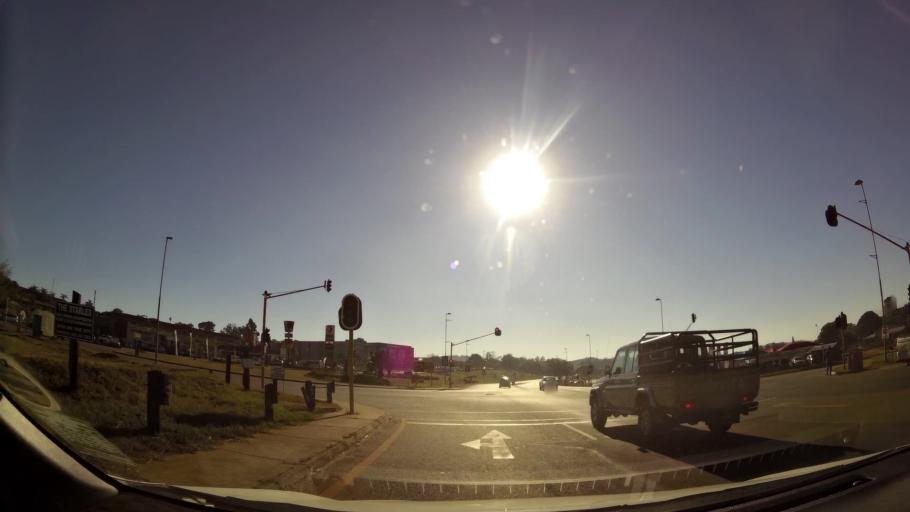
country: ZA
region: Limpopo
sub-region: Mopani District Municipality
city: Tzaneen
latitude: -23.8254
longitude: 30.1552
